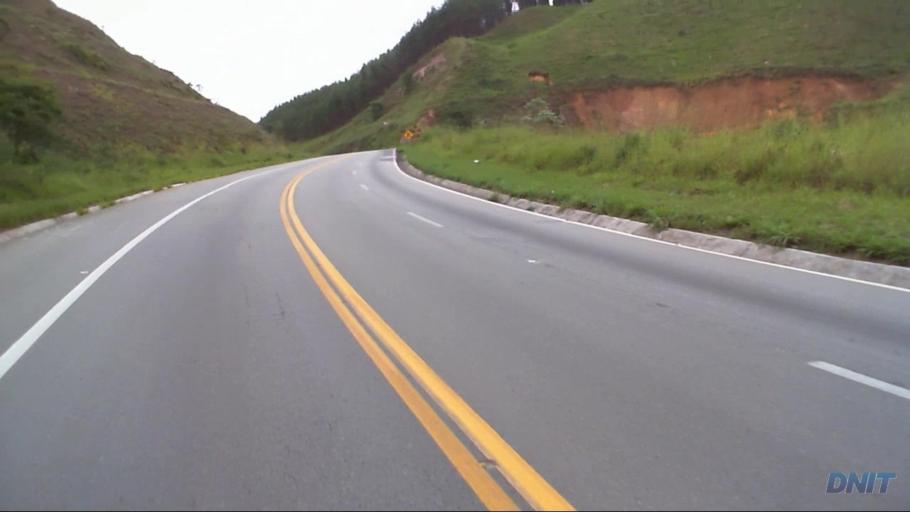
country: BR
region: Minas Gerais
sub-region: Nova Era
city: Nova Era
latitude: -19.6719
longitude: -42.9722
